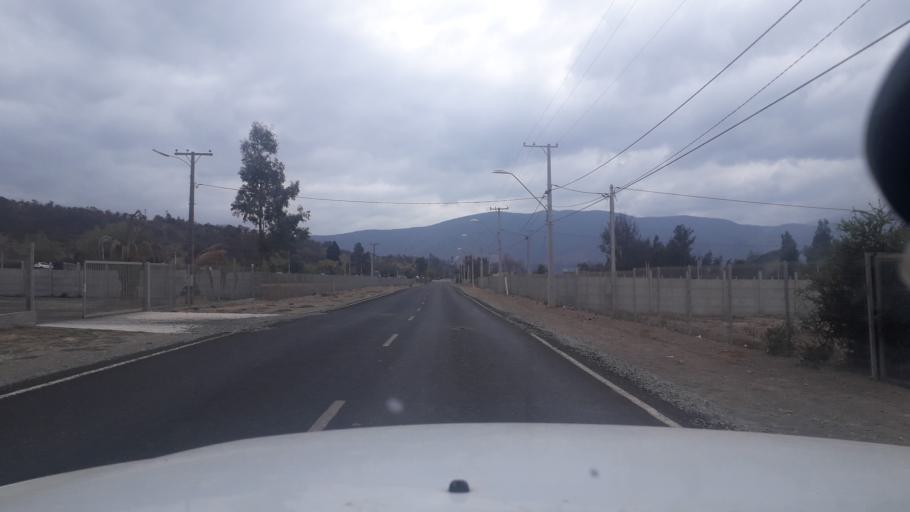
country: CL
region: Valparaiso
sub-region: Provincia de Marga Marga
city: Limache
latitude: -33.0214
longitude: -71.2740
